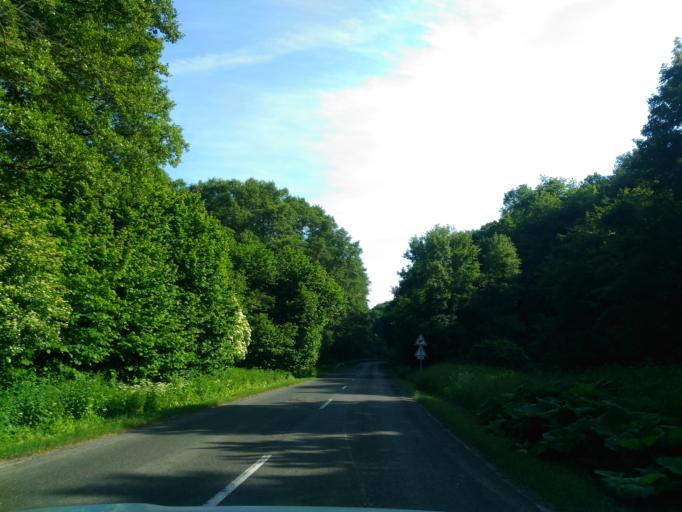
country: HU
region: Baranya
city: Komlo
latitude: 46.2244
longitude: 18.3040
